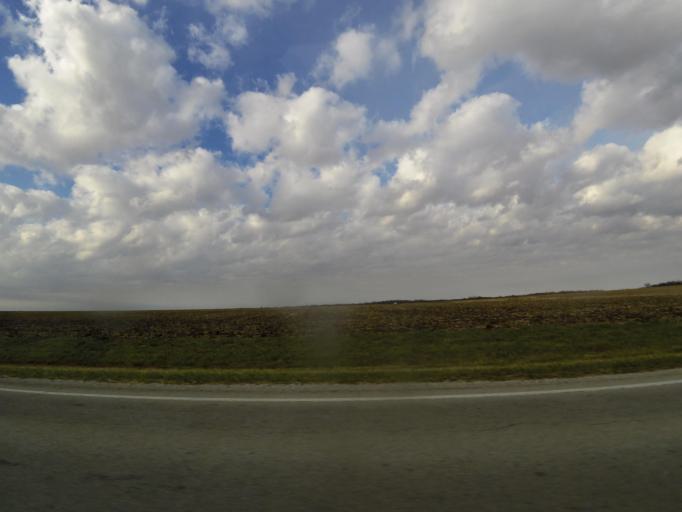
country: US
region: Illinois
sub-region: Fayette County
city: Ramsey
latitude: 39.2403
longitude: -89.1006
